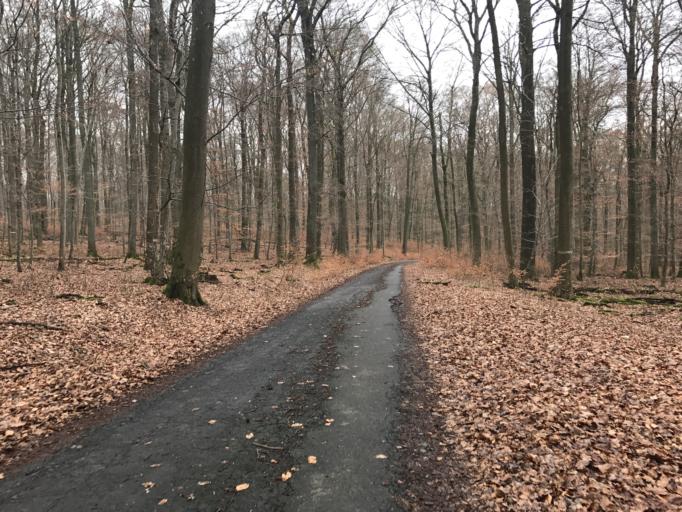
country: DE
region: Hesse
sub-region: Regierungsbezirk Darmstadt
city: Wiesbaden
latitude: 50.1243
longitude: 8.2337
